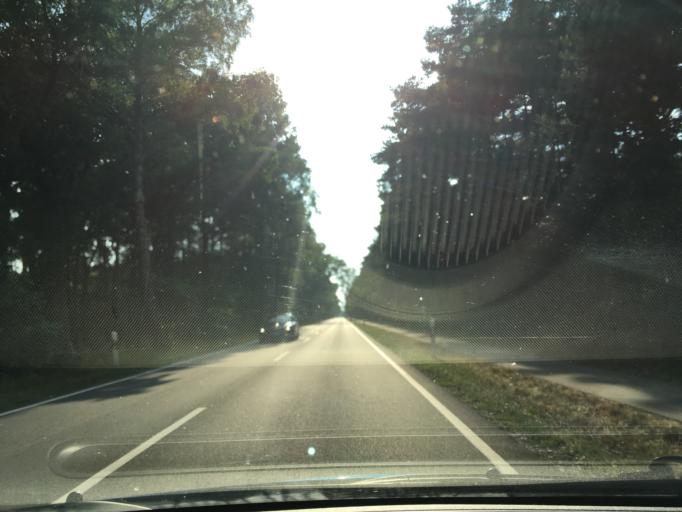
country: DE
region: Lower Saxony
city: Karwitz
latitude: 53.0845
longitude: 11.0447
